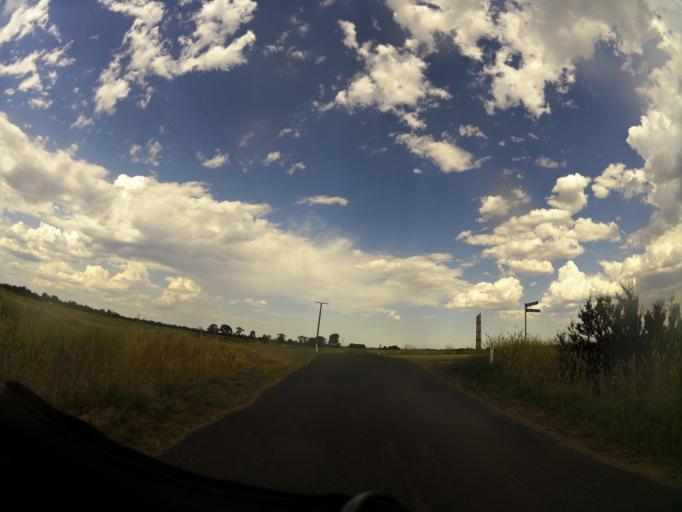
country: AU
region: Victoria
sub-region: Wellington
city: Heyfield
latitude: -37.9992
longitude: 146.6978
